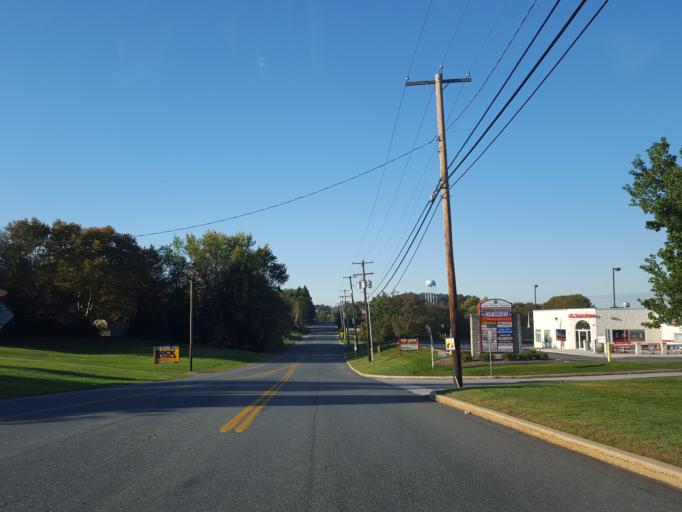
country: US
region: Pennsylvania
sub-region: York County
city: Yoe
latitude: 39.9155
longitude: -76.6304
